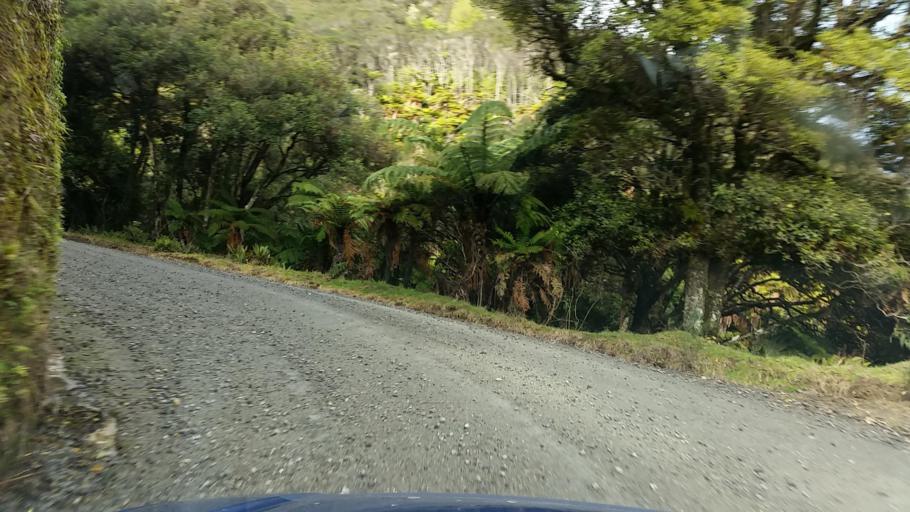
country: NZ
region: Taranaki
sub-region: South Taranaki District
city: Eltham
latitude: -39.2722
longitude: 174.7441
